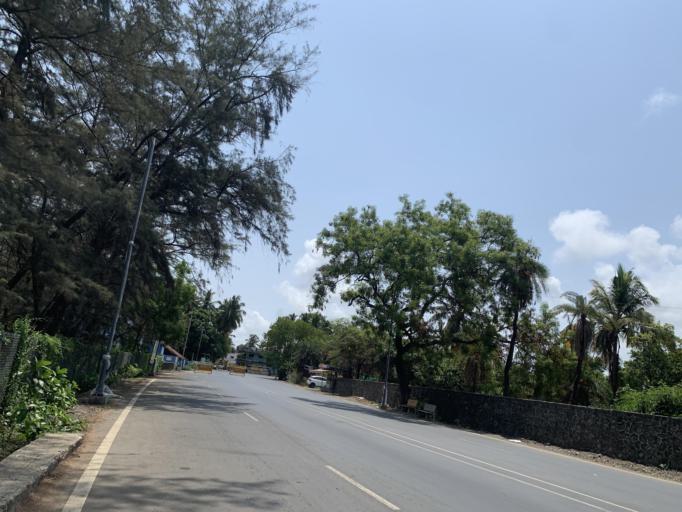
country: IN
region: Daman and Diu
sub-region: Daman District
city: Daman
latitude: 20.4634
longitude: 72.8519
